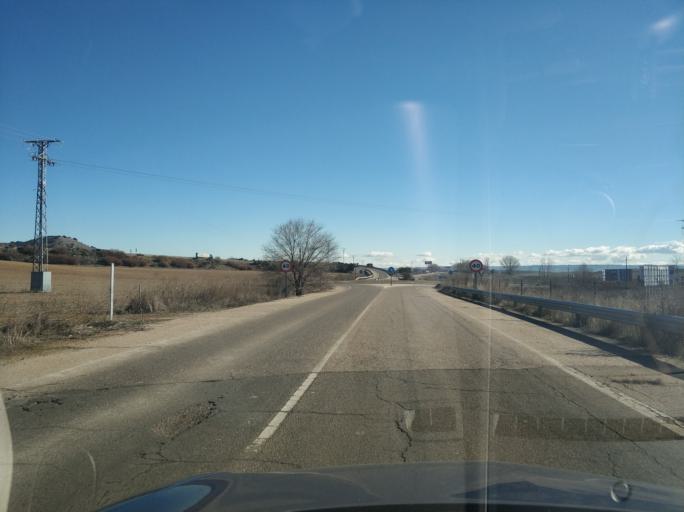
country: ES
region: Castille and Leon
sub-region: Provincia de Valladolid
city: Cisterniga
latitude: 41.6004
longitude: -4.6655
